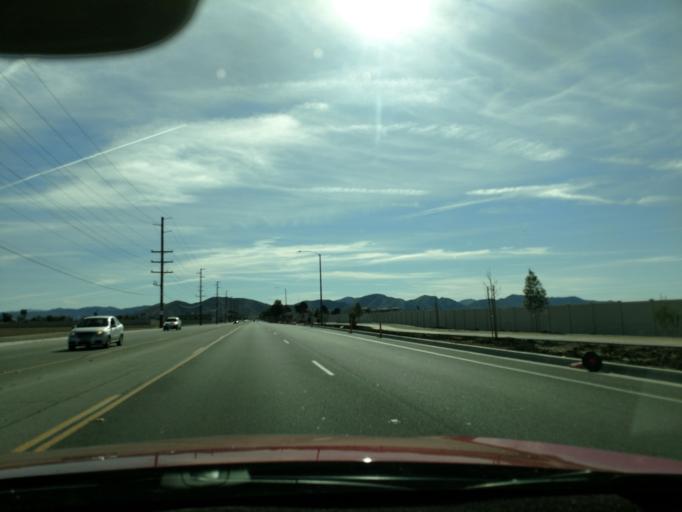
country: US
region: California
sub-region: Riverside County
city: Hemet
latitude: 33.7403
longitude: -117.0067
